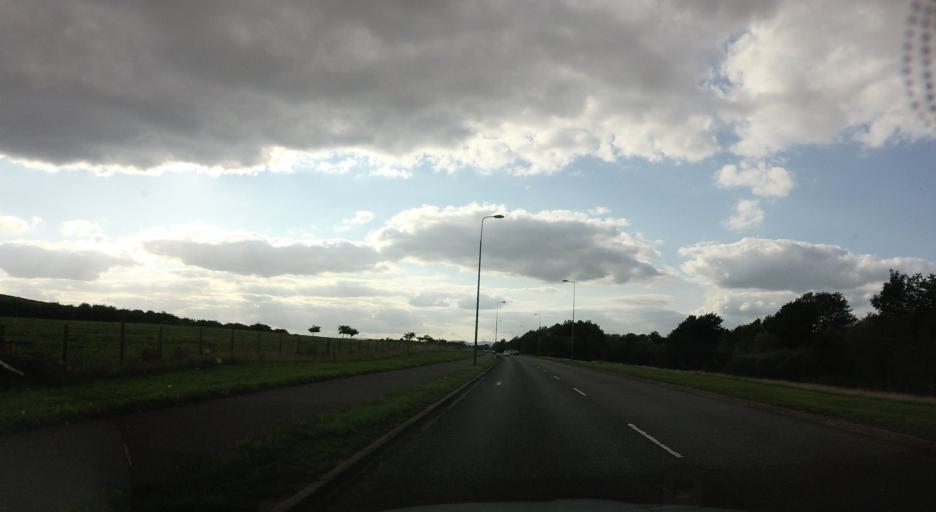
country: GB
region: Scotland
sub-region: Angus
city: Muirhead
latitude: 56.4575
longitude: -3.0414
